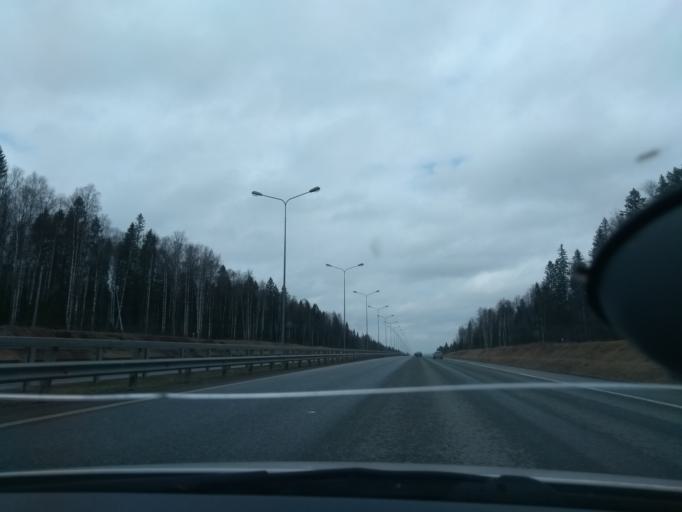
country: RU
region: Perm
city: Zvezdnyy
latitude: 57.7537
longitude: 56.3333
